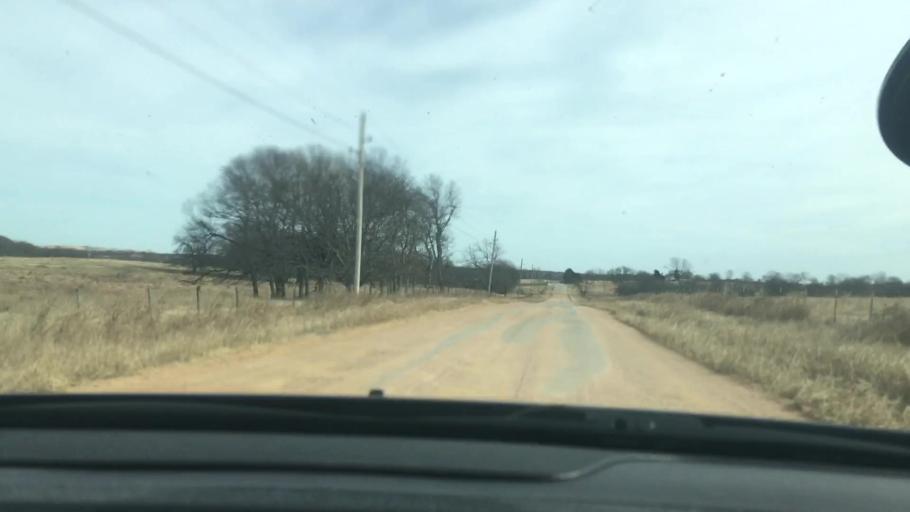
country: US
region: Oklahoma
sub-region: Murray County
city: Sulphur
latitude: 34.4050
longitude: -96.8902
